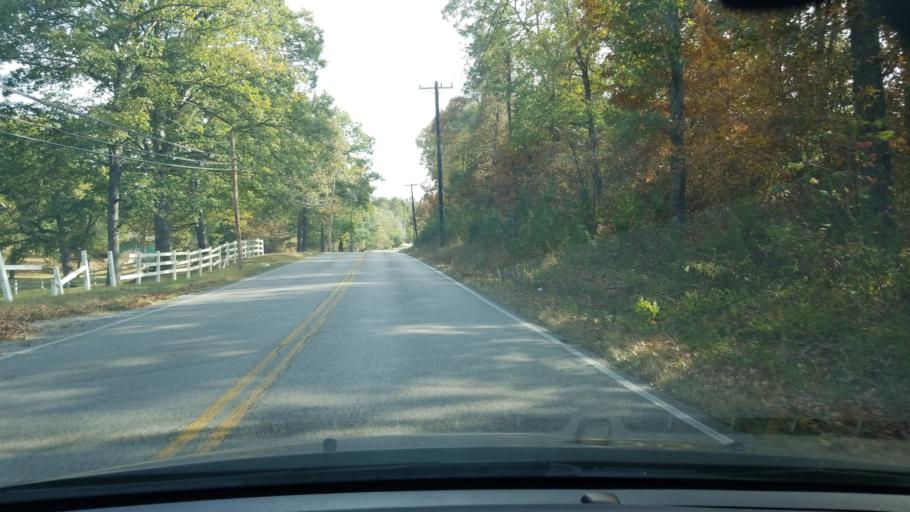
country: US
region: Tennessee
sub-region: Cumberland County
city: Crossville
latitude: 35.9781
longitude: -85.0356
